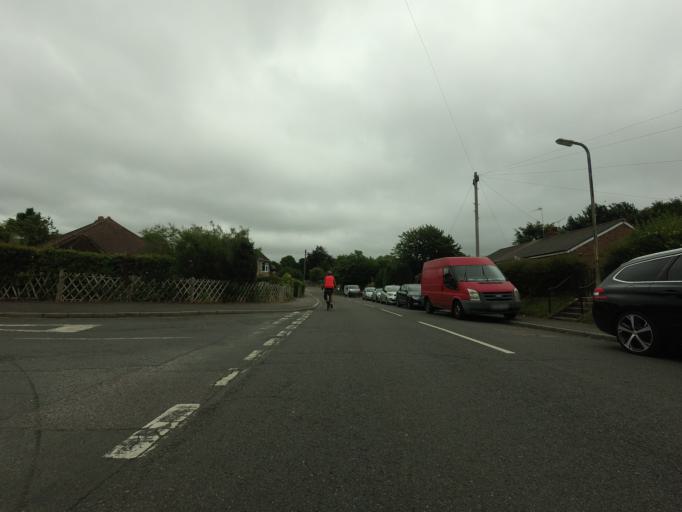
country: GB
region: England
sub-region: Kent
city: Meopham
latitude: 51.3758
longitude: 0.3583
